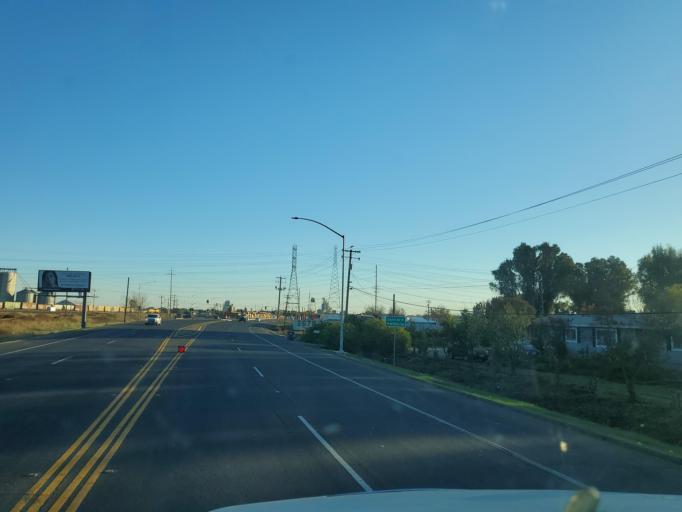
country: US
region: California
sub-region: San Joaquin County
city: Taft Mosswood
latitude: 37.9130
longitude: -121.2764
